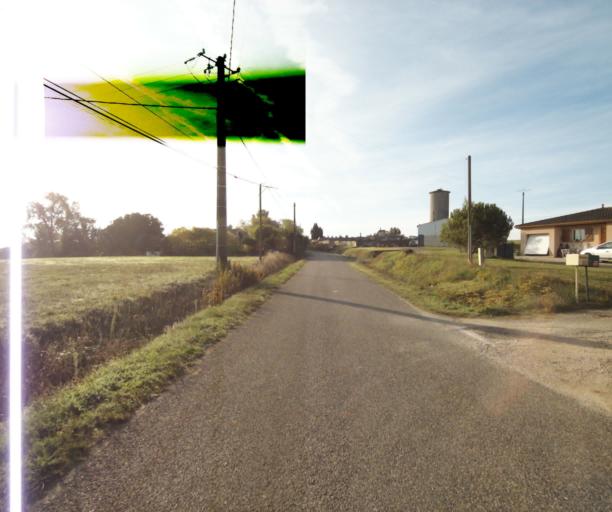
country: FR
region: Midi-Pyrenees
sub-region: Departement de la Haute-Garonne
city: Villemur-sur-Tarn
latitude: 43.9049
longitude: 1.4923
